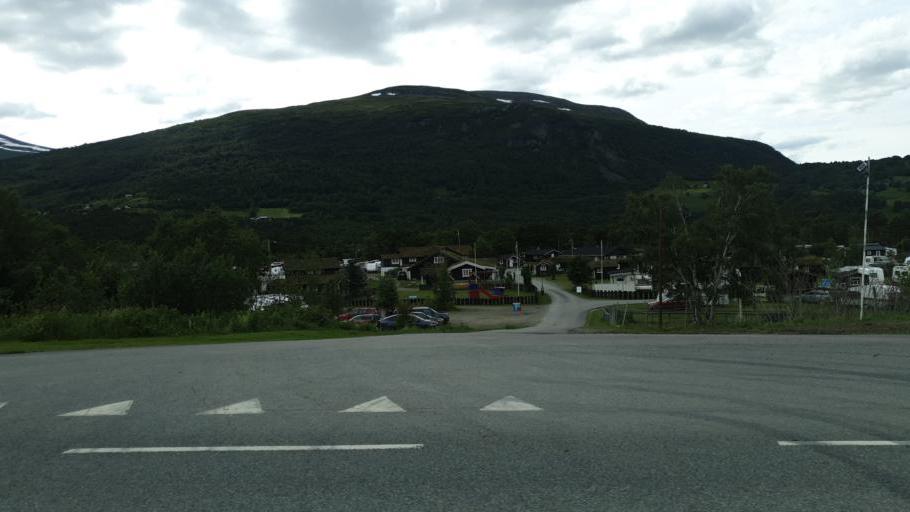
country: NO
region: Sor-Trondelag
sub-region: Oppdal
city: Oppdal
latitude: 62.5476
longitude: 9.6318
